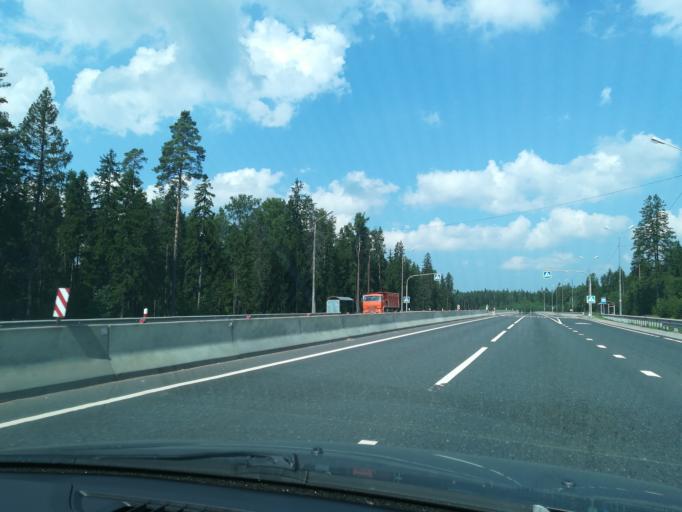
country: RU
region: Leningrad
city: Vistino
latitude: 59.6407
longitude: 28.5711
